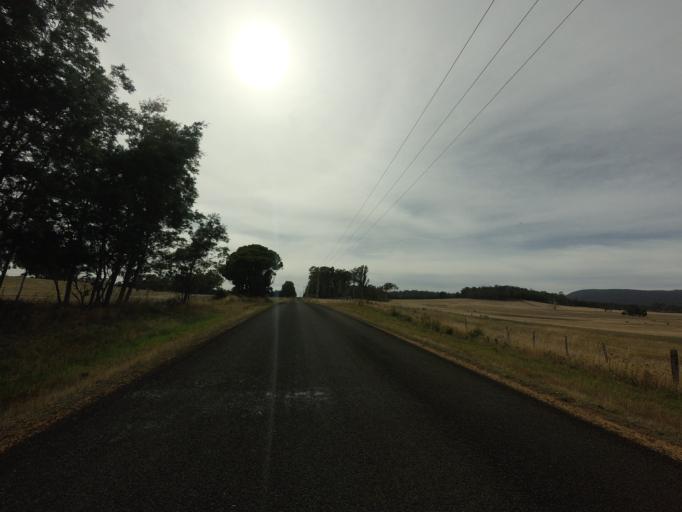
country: AU
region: Tasmania
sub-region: Sorell
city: Sorell
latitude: -42.4290
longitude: 147.4723
